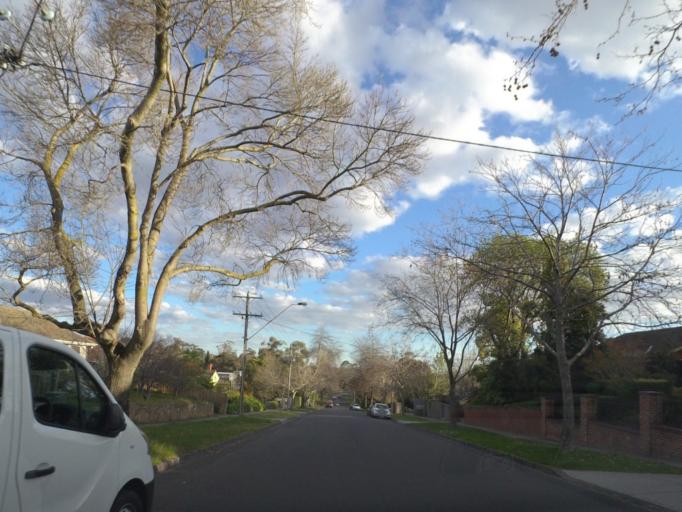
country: AU
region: Victoria
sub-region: Whitehorse
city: Surrey Hills
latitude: -37.8295
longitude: 145.0966
